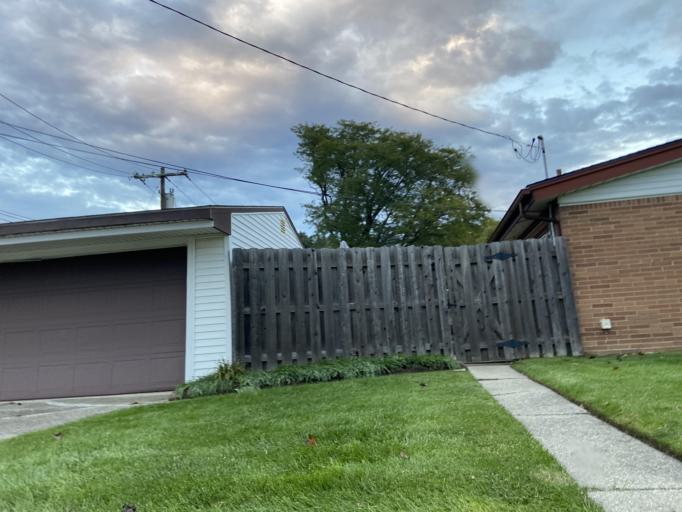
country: US
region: Michigan
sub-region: Wayne County
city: Livonia
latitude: 42.3638
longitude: -83.3285
